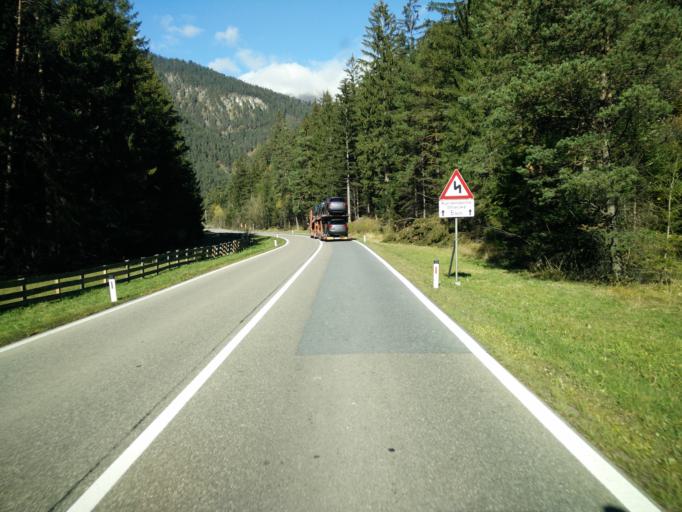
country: AT
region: Tyrol
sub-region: Politischer Bezirk Imst
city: Nassereith
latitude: 47.3360
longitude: 10.8189
